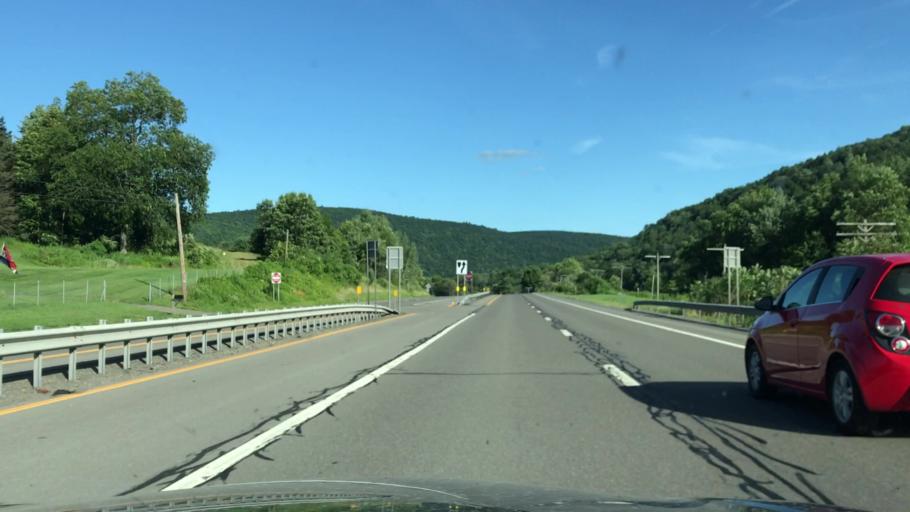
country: US
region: New York
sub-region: Delaware County
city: Hancock
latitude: 42.0008
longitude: -75.3564
